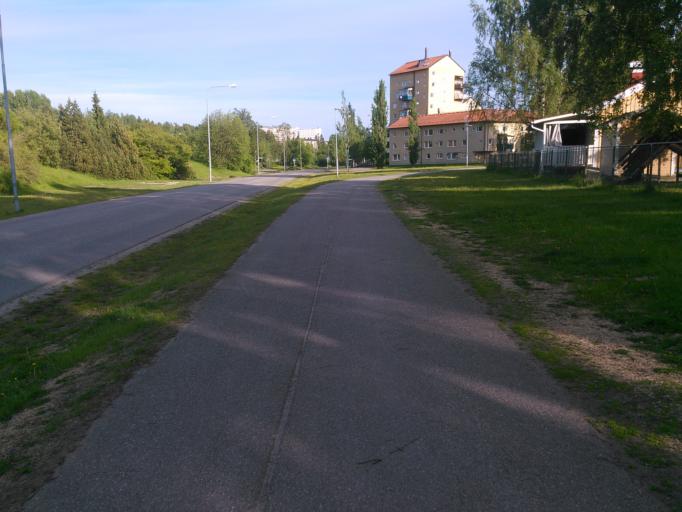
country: SE
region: Vaesterbotten
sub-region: Umea Kommun
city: Umea
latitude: 63.8252
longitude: 20.2861
